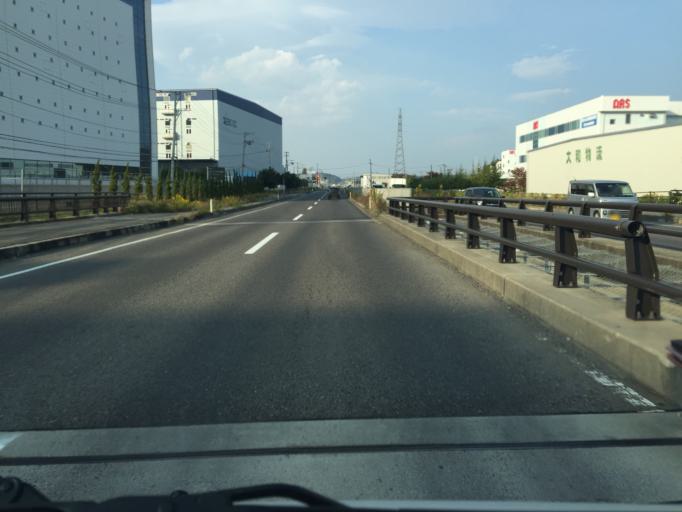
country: JP
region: Fukushima
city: Motomiya
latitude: 37.5256
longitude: 140.3959
